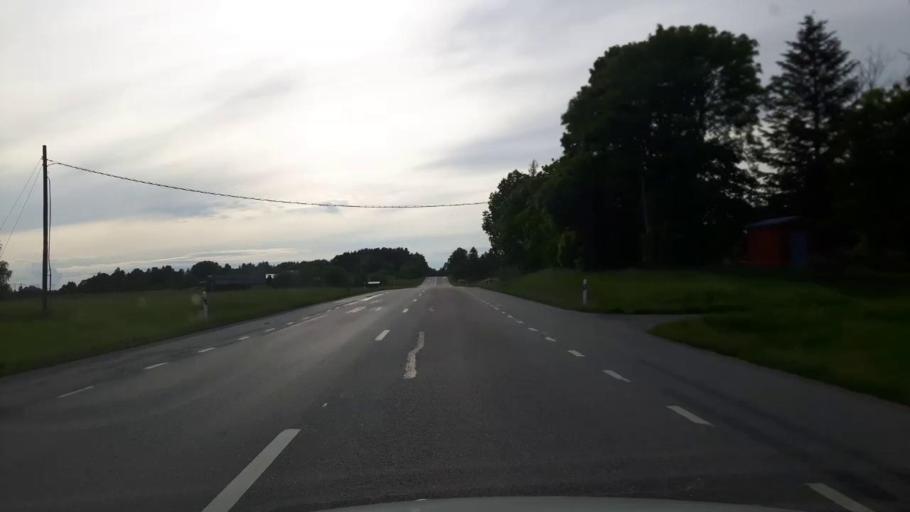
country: SE
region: Uppsala
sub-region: Enkopings Kommun
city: Orsundsbro
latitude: 59.6591
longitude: 17.3358
